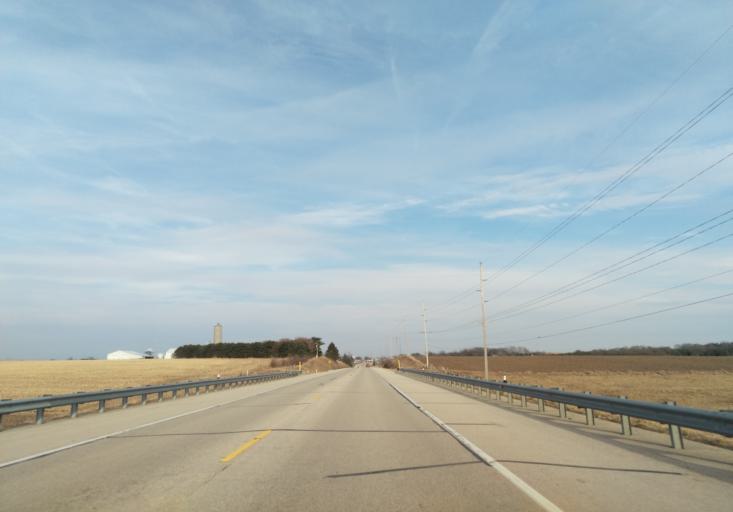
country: US
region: Wisconsin
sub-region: Iowa County
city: Dodgeville
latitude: 42.9747
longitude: -90.1622
